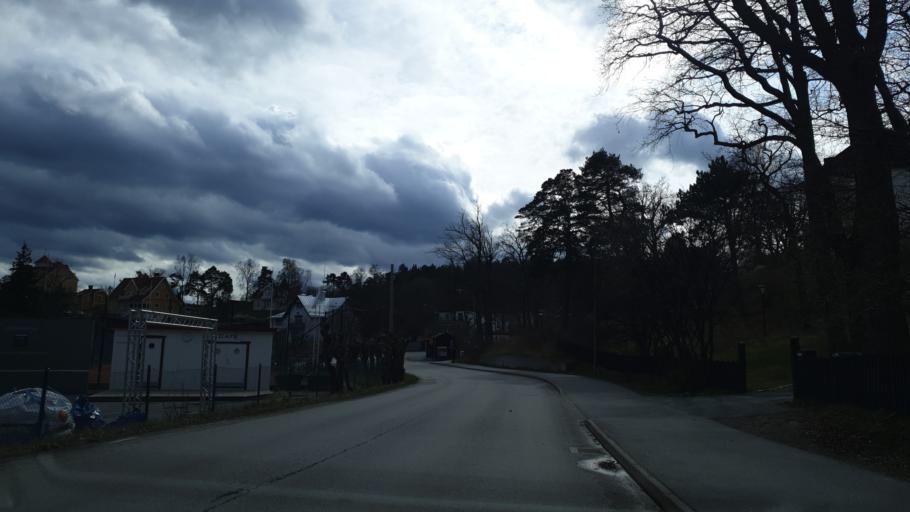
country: SE
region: Stockholm
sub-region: Nacka Kommun
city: Saltsjobaden
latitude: 59.2745
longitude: 18.3098
